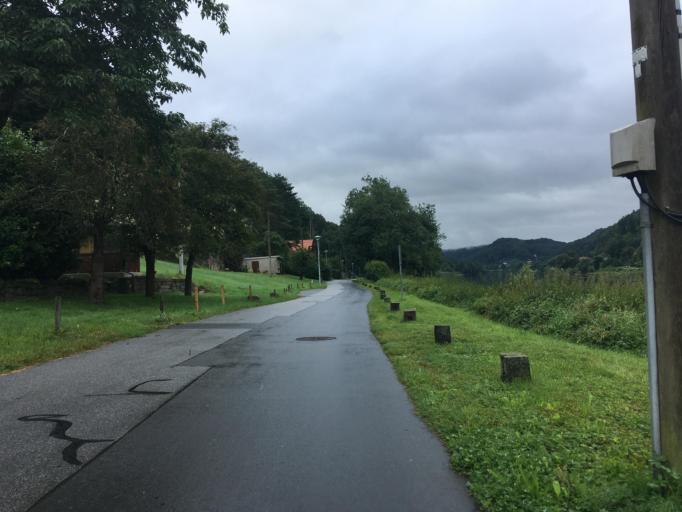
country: DE
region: Saxony
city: Pirna
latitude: 50.9620
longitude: 13.9696
